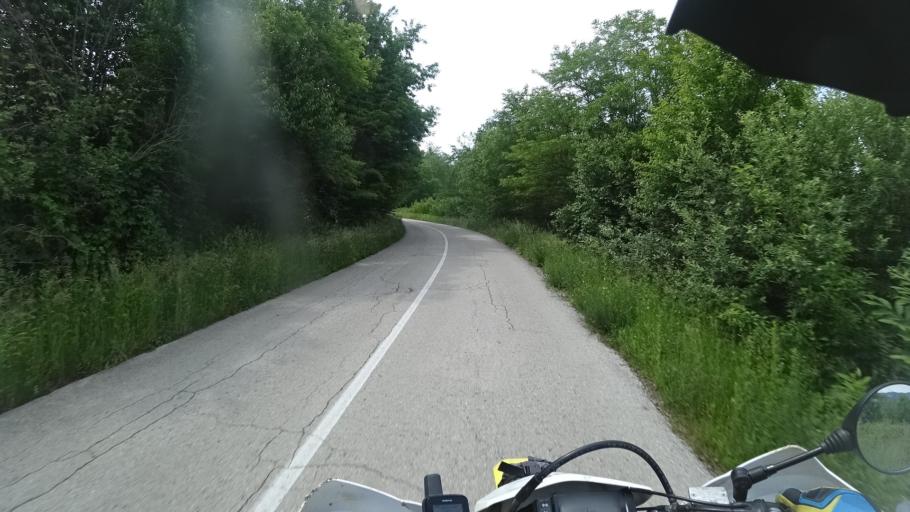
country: HR
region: Sisacko-Moslavacka
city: Gvozd
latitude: 45.3416
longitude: 15.8597
